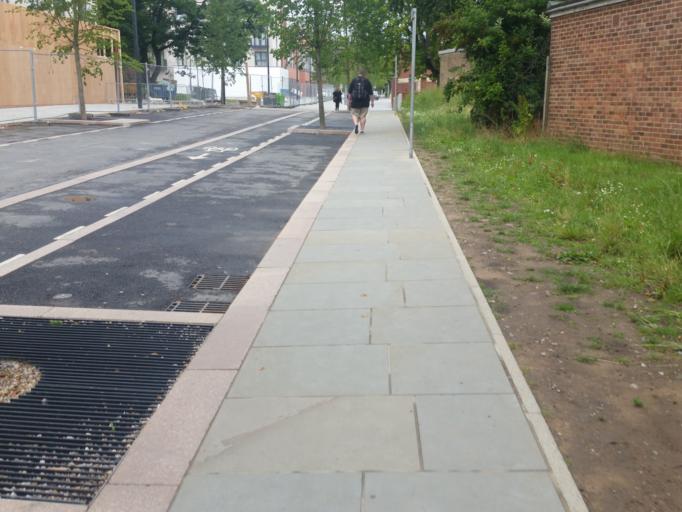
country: GB
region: England
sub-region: Derby
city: Derby
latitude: 52.9173
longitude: -1.4668
